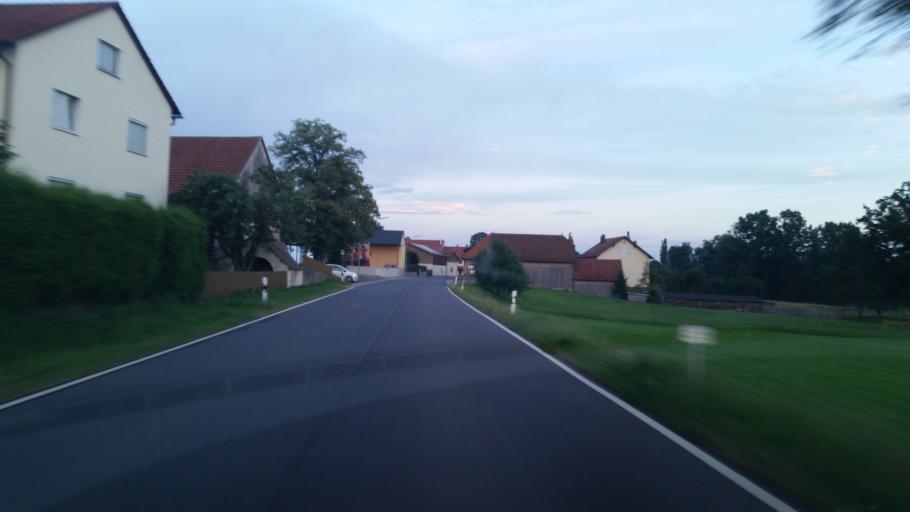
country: DE
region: Bavaria
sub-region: Upper Palatinate
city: Wernberg-Koblitz
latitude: 49.5538
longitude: 12.1406
